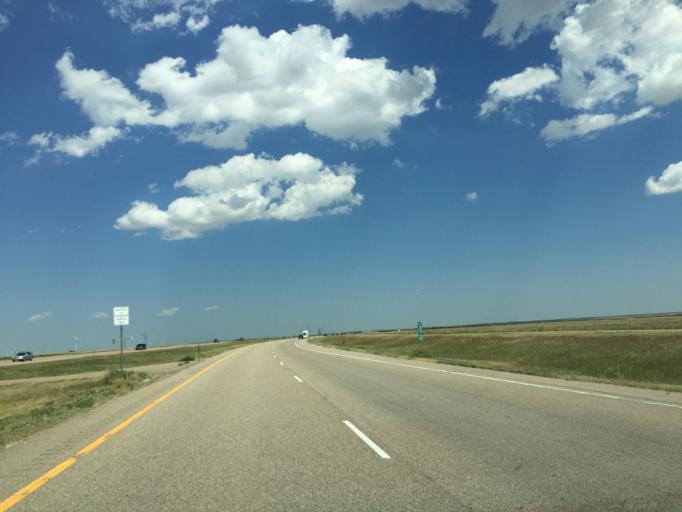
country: US
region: Colorado
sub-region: Lincoln County
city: Hugo
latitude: 39.2760
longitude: -103.4826
